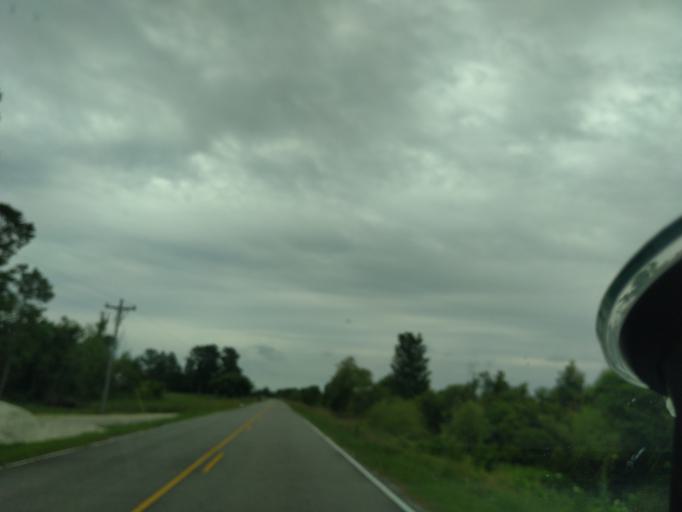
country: US
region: North Carolina
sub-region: Beaufort County
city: Belhaven
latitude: 35.7538
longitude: -76.5132
